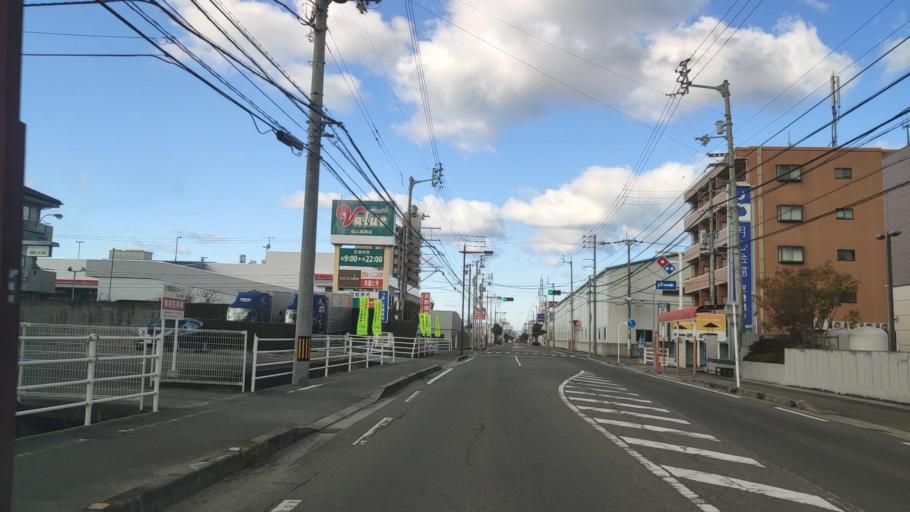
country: JP
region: Ehime
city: Masaki-cho
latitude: 33.8283
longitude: 132.7224
